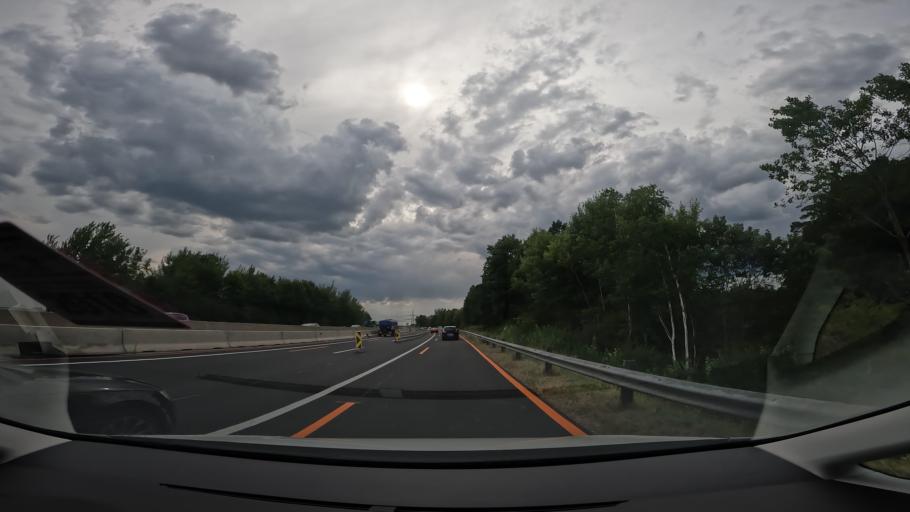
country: AT
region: Styria
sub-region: Politischer Bezirk Hartberg-Fuerstenfeld
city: Sankt Johann in der Haide
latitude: 47.2731
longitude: 16.0160
